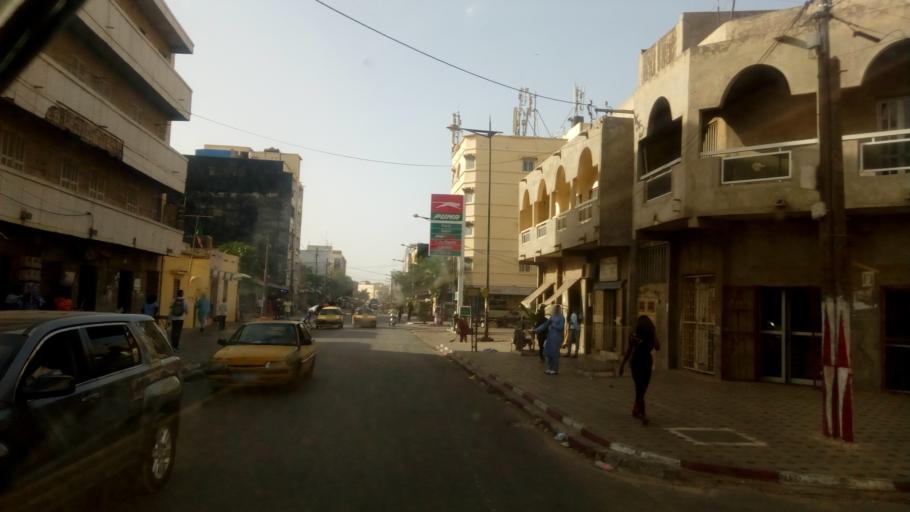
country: SN
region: Dakar
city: Dakar
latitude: 14.6849
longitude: -17.4491
